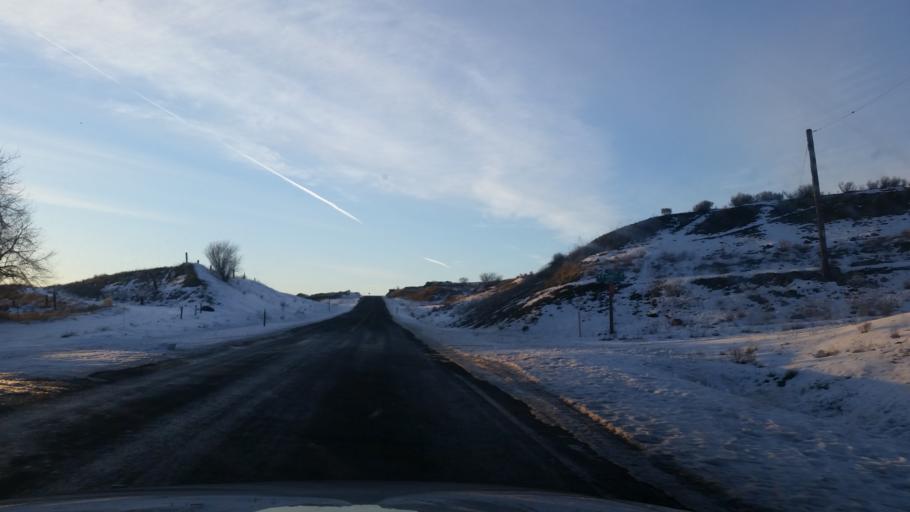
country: US
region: Washington
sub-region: Spokane County
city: Cheney
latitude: 47.1170
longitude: -117.7342
